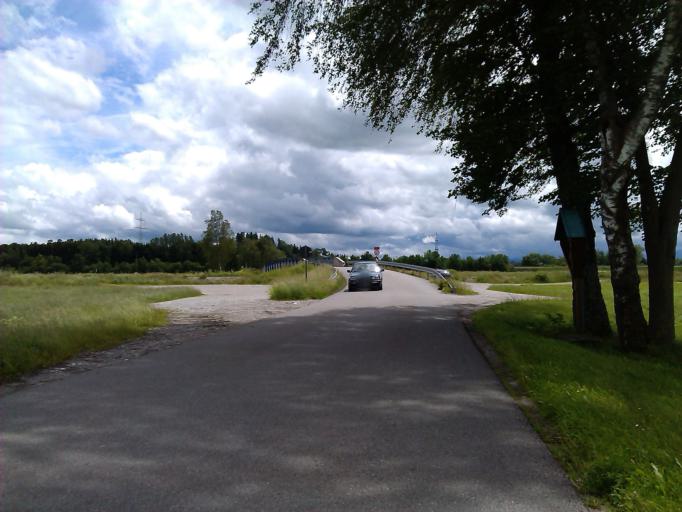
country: DE
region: Bavaria
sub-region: Swabia
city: Marktoberdorf
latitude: 47.8057
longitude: 10.6220
